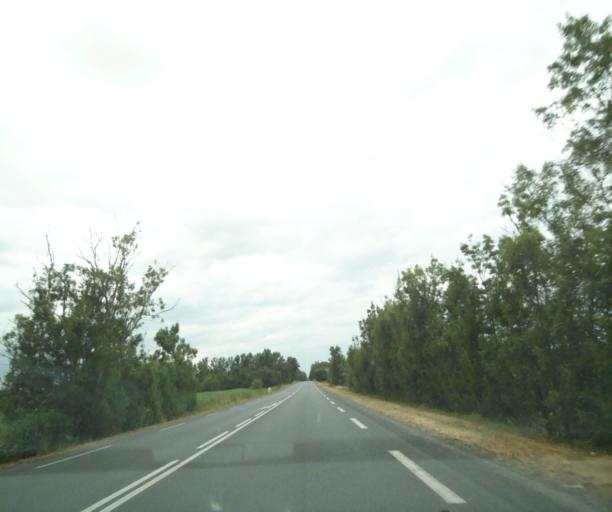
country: FR
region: Pays de la Loire
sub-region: Departement de la Vendee
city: Sainte-Gemme-la-Plaine
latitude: 46.4375
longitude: -1.0998
